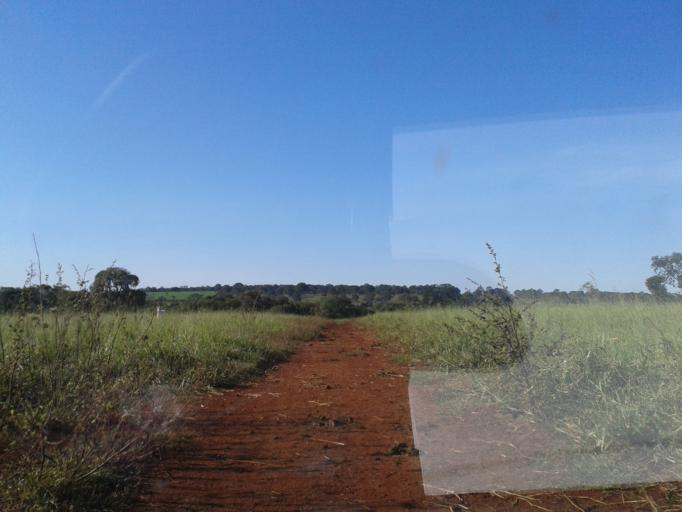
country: BR
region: Minas Gerais
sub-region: Santa Vitoria
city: Santa Vitoria
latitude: -18.9944
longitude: -50.3514
